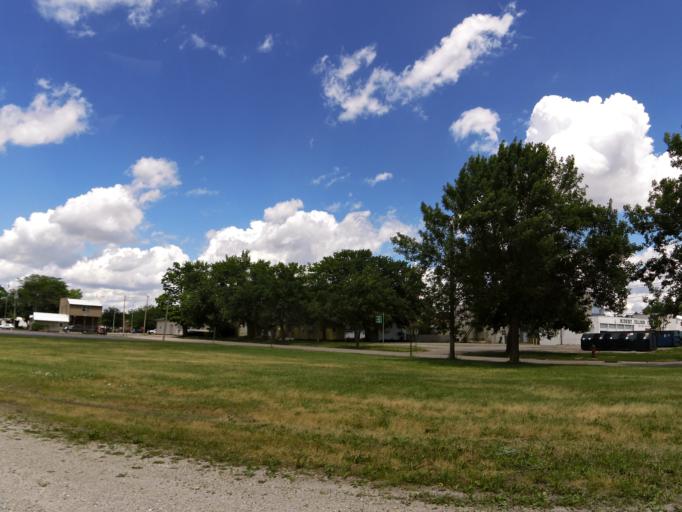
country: US
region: Iowa
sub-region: Fayette County
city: Oelwein
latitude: 42.6756
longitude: -91.9150
